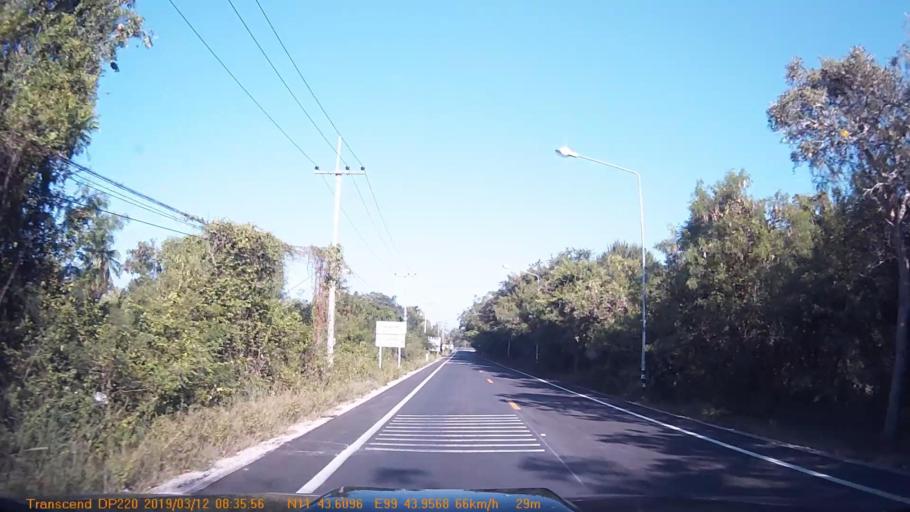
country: TH
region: Prachuap Khiri Khan
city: Prachuap Khiri Khan
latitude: 11.7270
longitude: 99.7323
